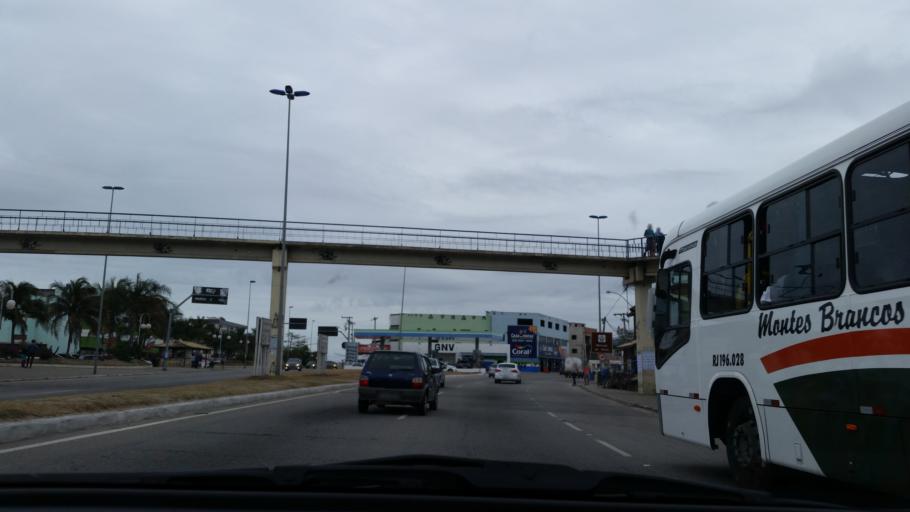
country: BR
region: Rio de Janeiro
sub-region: Sao Pedro Da Aldeia
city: Sao Pedro da Aldeia
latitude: -22.8346
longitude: -42.1007
